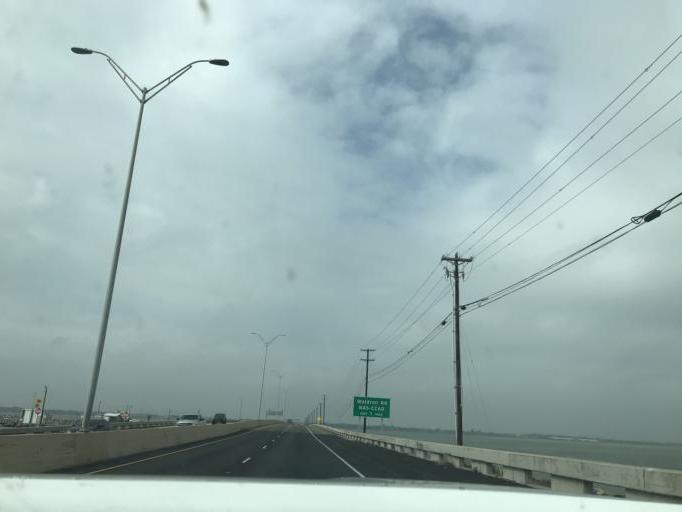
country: US
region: Texas
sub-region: Nueces County
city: Corpus Christi
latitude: 27.6571
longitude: -97.2590
